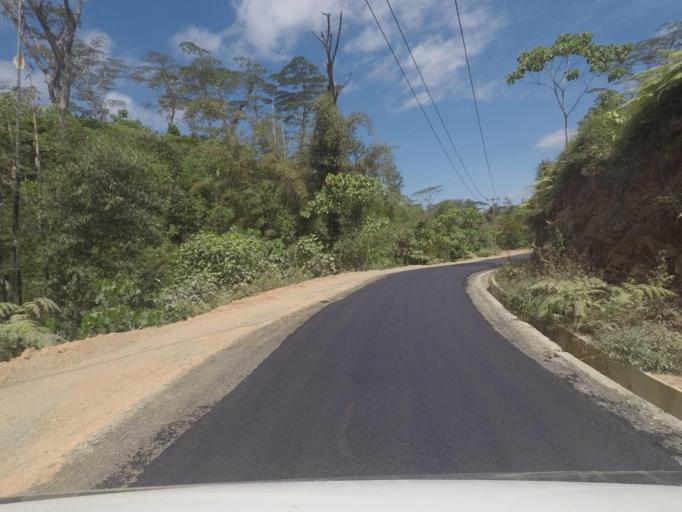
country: TL
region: Ermera
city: Gleno
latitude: -8.7507
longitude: 125.3402
